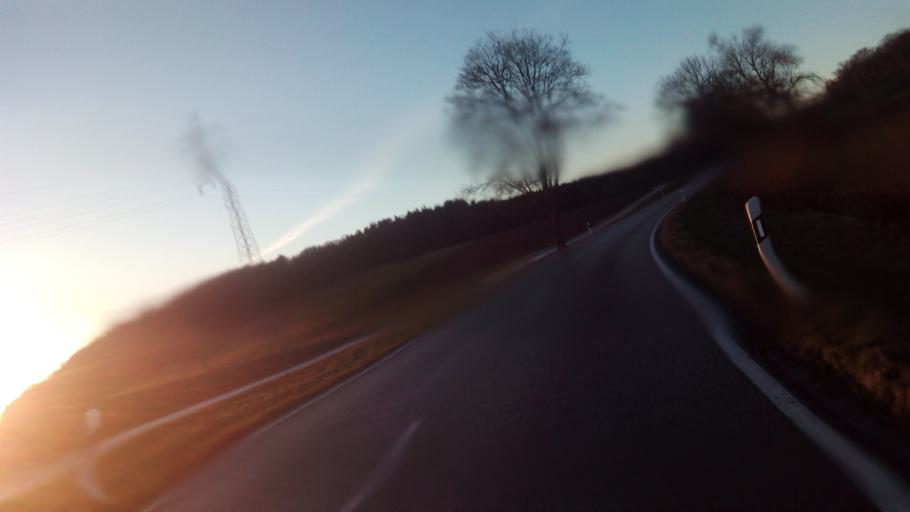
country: DE
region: Baden-Wuerttemberg
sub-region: Tuebingen Region
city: Oberdischingen
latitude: 48.3327
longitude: 9.8444
